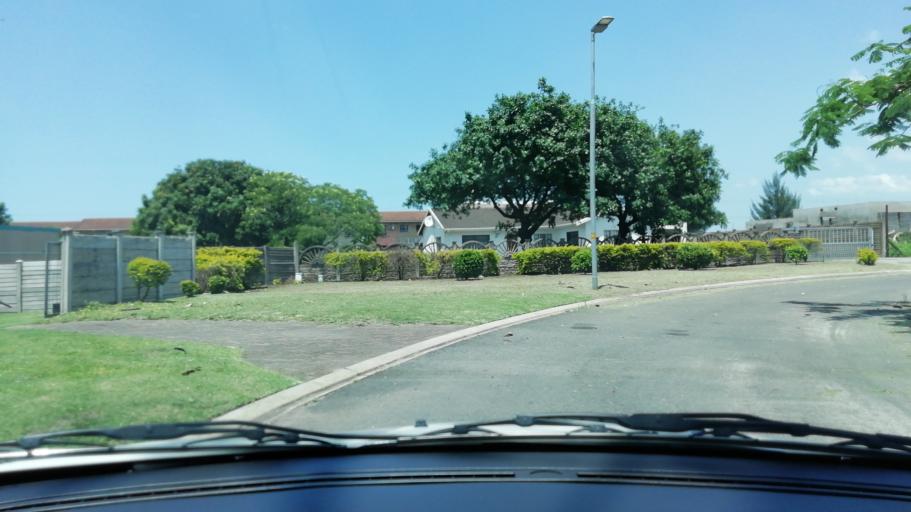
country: ZA
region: KwaZulu-Natal
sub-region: uThungulu District Municipality
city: Richards Bay
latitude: -28.7371
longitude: 32.0471
